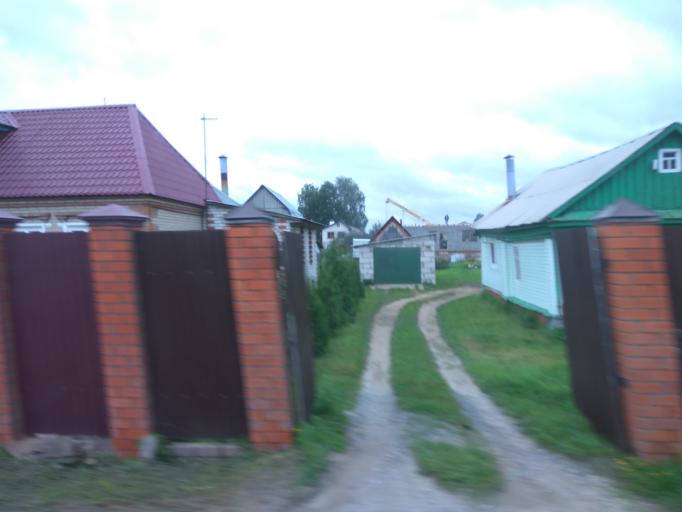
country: RU
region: Moskovskaya
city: Malyshevo
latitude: 55.4992
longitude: 38.3472
